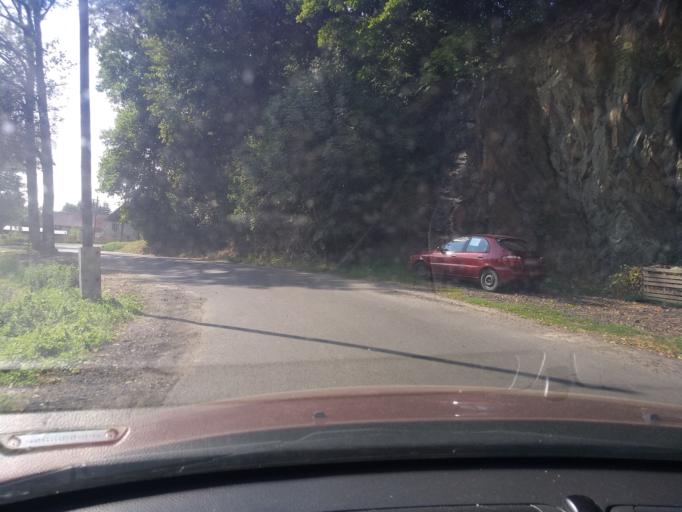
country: PL
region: Lower Silesian Voivodeship
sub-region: Powiat lubanski
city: Siekierczyn
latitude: 51.0751
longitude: 15.1551
